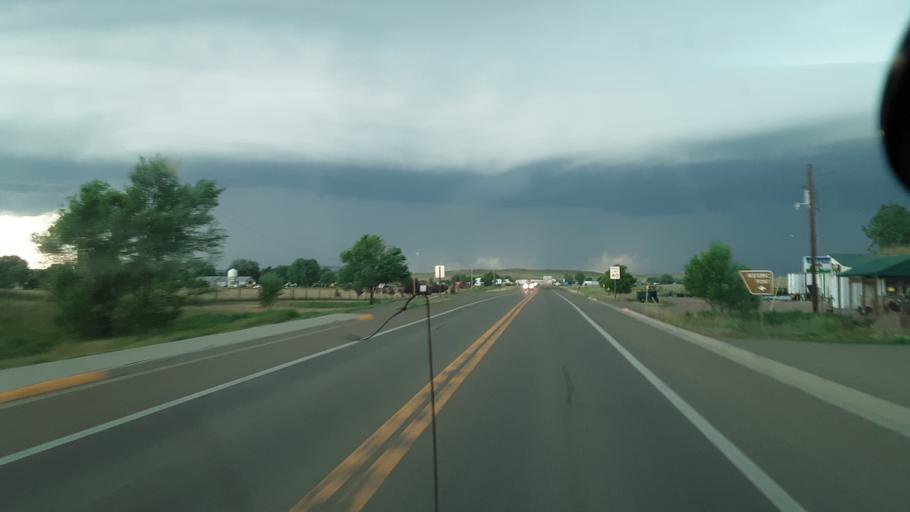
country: US
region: Montana
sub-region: Powder River County
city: Broadus
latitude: 45.4435
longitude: -105.4119
